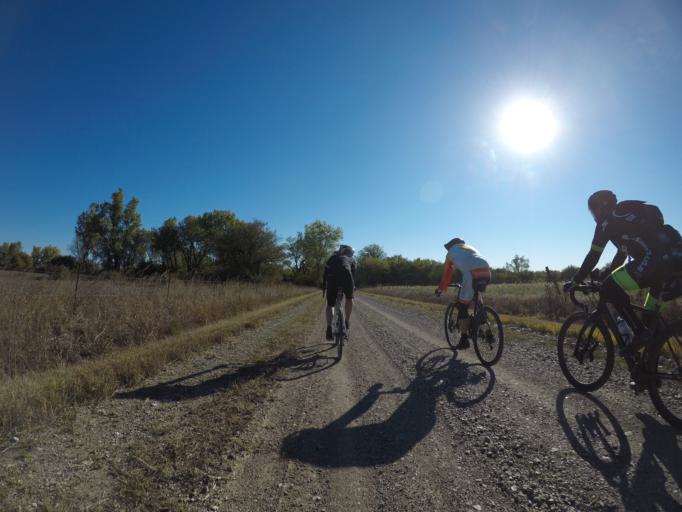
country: US
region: Kansas
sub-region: Morris County
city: Council Grove
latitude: 38.8256
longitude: -96.4318
